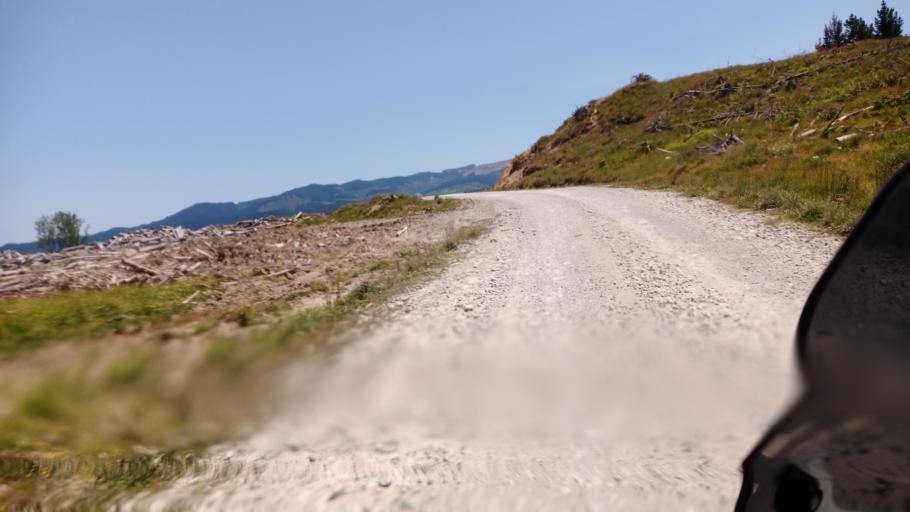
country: NZ
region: Gisborne
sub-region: Gisborne District
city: Gisborne
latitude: -38.2911
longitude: 178.0177
